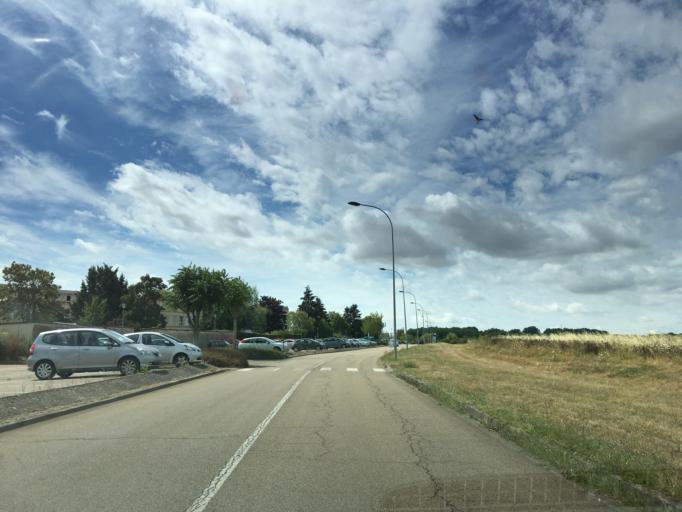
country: FR
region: Bourgogne
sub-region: Departement de l'Yonne
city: Auxerre
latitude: 47.8112
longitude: 3.5544
